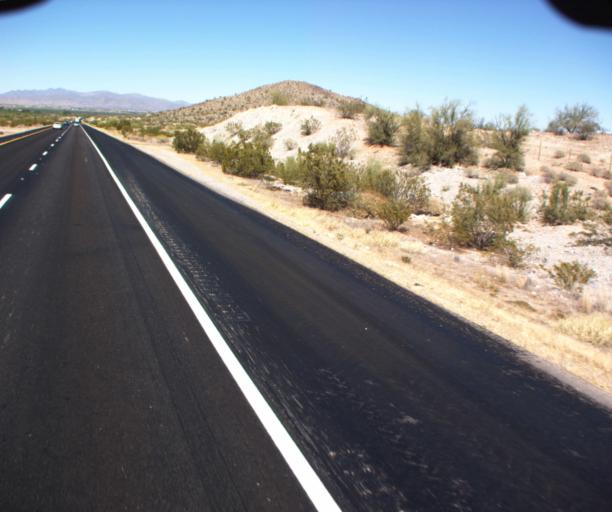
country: US
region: Arizona
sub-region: Maricopa County
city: Buckeye
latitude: 33.3014
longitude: -112.6265
